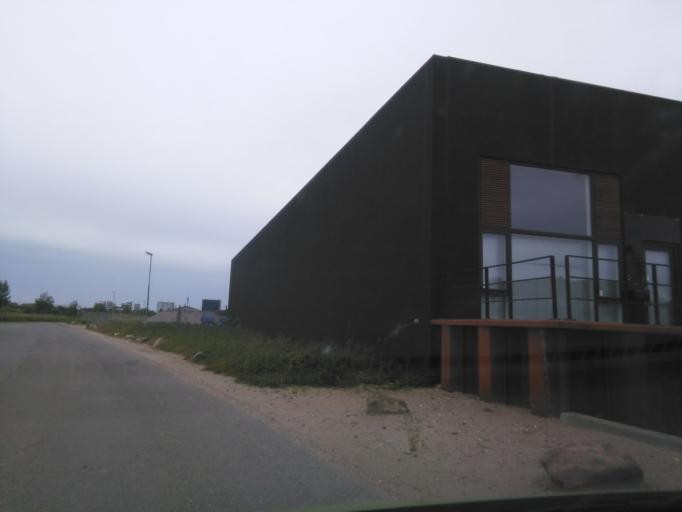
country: DK
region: Central Jutland
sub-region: Horsens Kommune
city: Horsens
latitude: 55.8543
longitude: 9.8659
